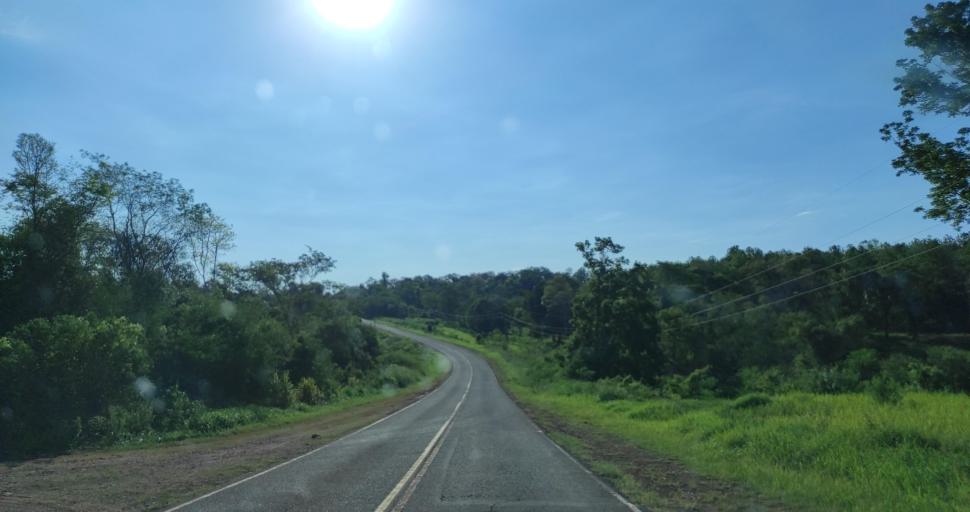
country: AR
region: Misiones
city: San Vicente
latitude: -26.3729
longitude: -54.3172
